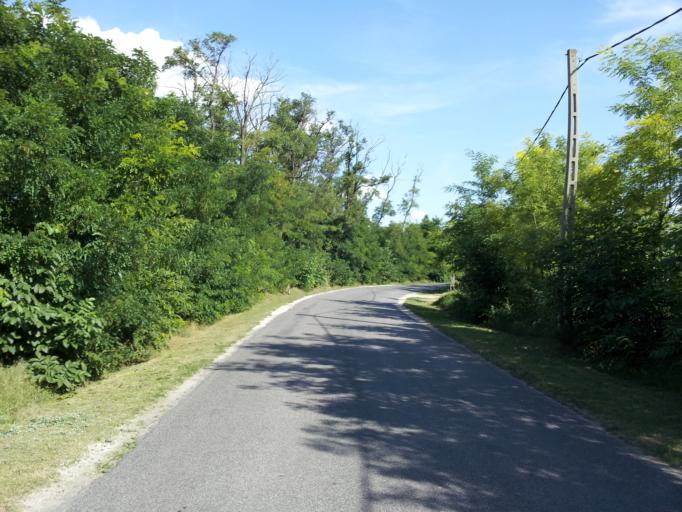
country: HU
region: Pest
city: Kiskunlachaza
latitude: 47.2182
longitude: 19.0138
